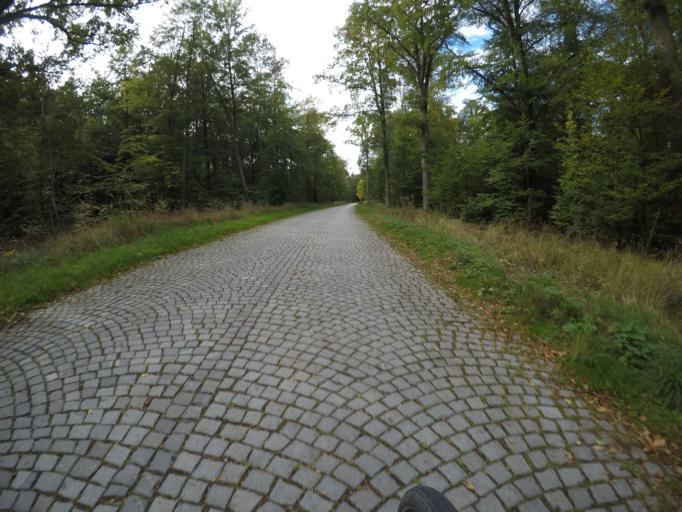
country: DE
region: Baden-Wuerttemberg
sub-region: Regierungsbezirk Stuttgart
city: Schonaich
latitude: 48.7090
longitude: 9.0783
